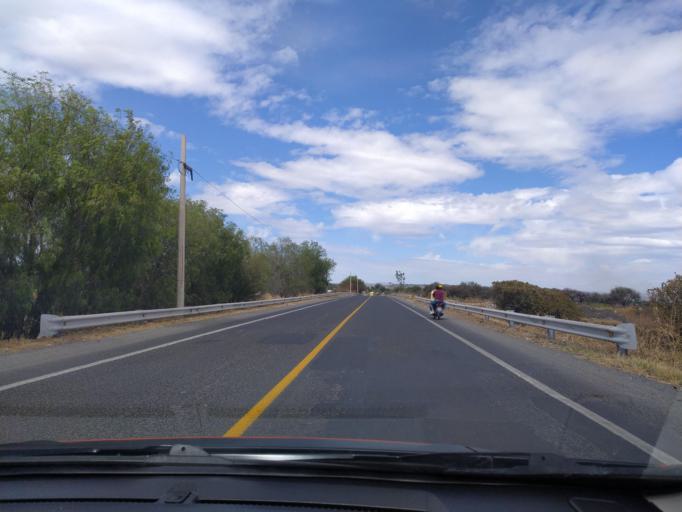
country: LA
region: Oudomxai
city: Muang La
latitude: 21.0078
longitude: 101.8299
